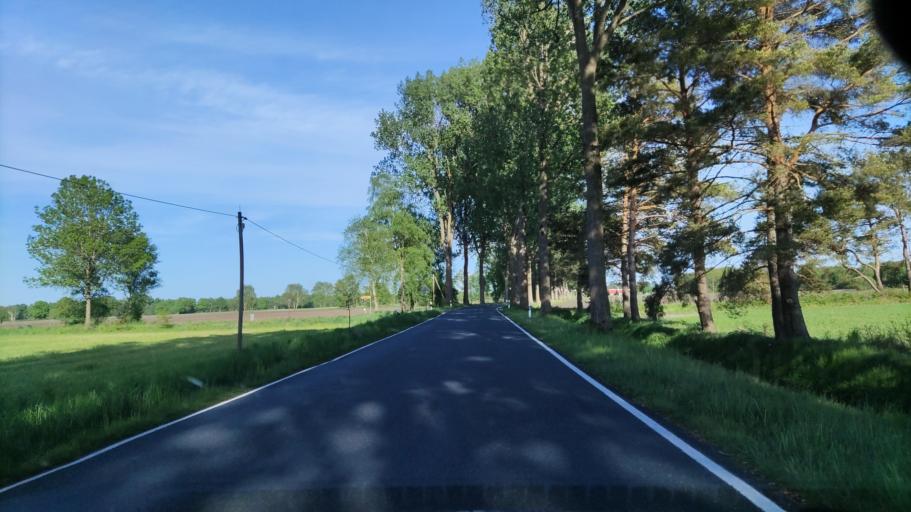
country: DE
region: Lower Saxony
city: Konigsmoor
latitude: 53.2242
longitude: 9.6942
